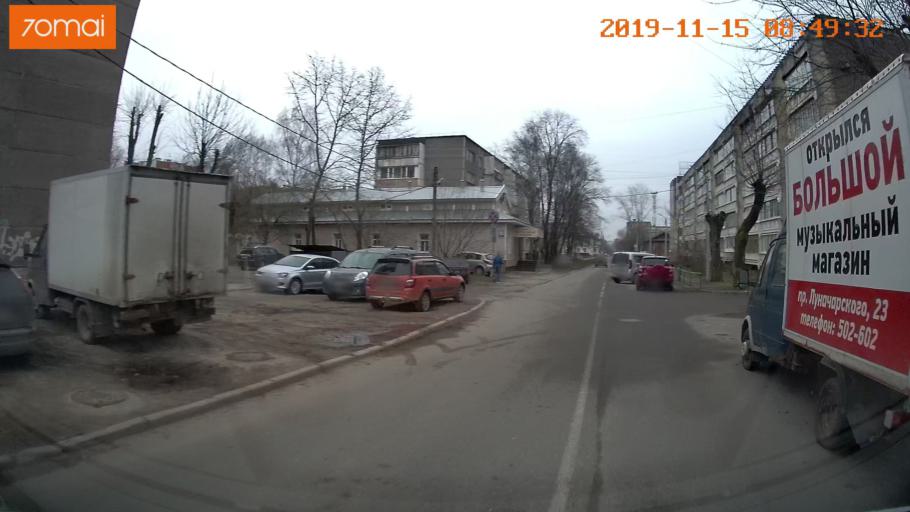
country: RU
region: Vologda
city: Cherepovets
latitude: 59.1237
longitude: 37.9223
